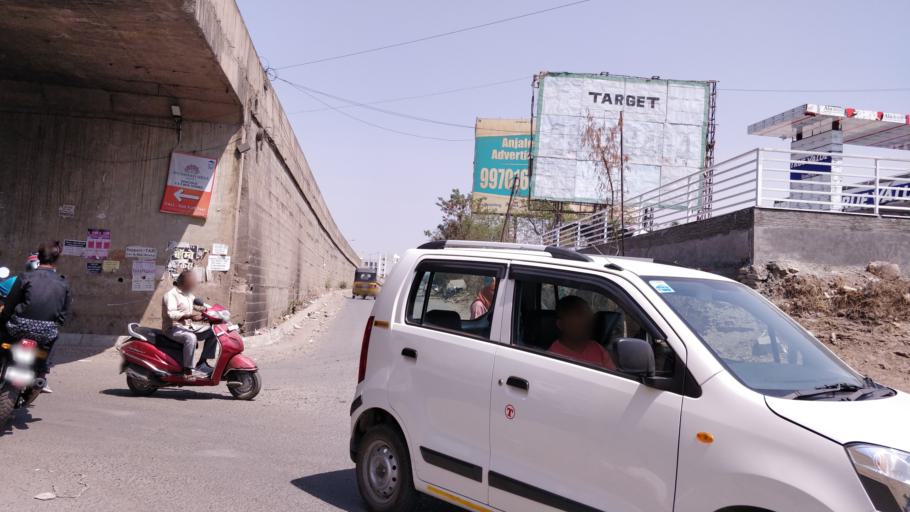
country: IN
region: Maharashtra
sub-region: Pune Division
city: Kharakvasla
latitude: 18.5158
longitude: 73.7692
